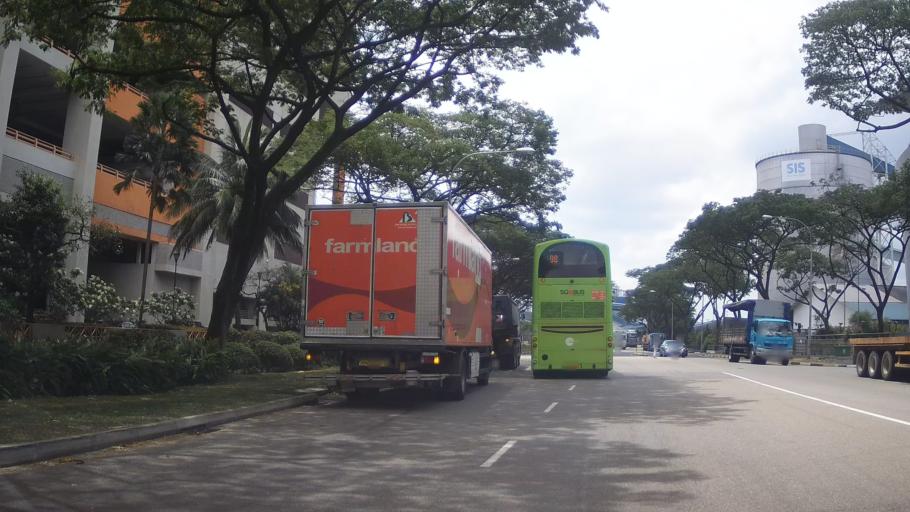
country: SG
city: Singapore
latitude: 1.3134
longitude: 103.7194
